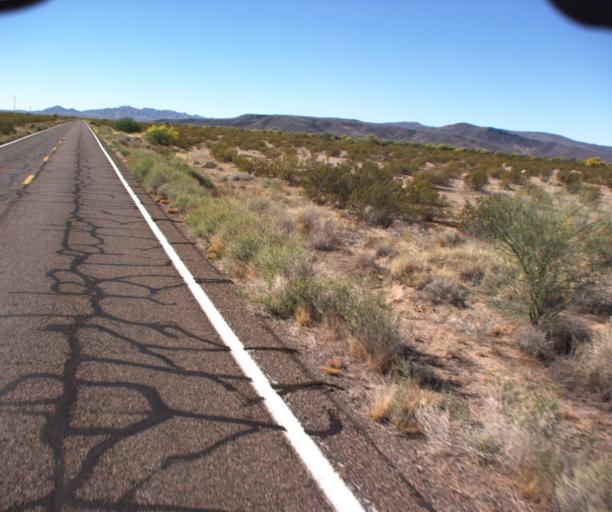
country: US
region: Arizona
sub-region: Pima County
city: Ajo
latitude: 32.5222
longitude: -112.8805
